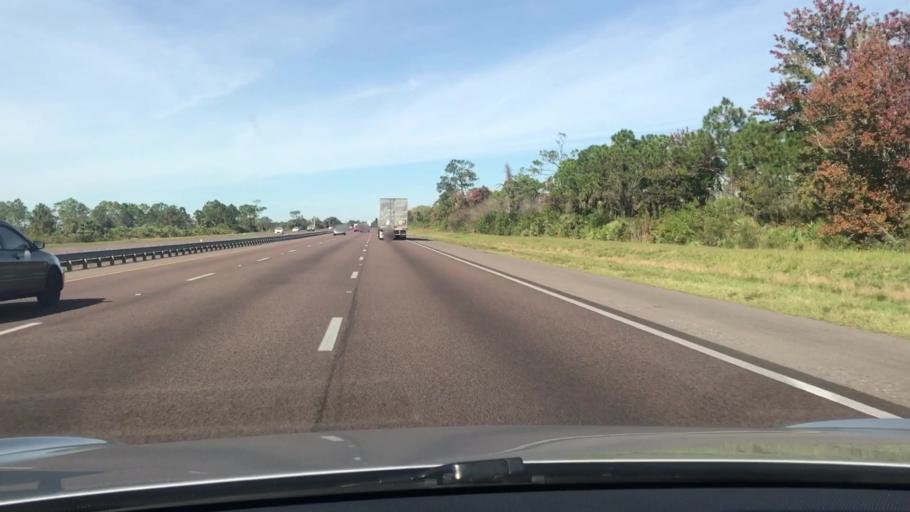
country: US
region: Florida
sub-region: Brevard County
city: Grant-Valkaria
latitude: 27.8560
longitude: -80.5853
